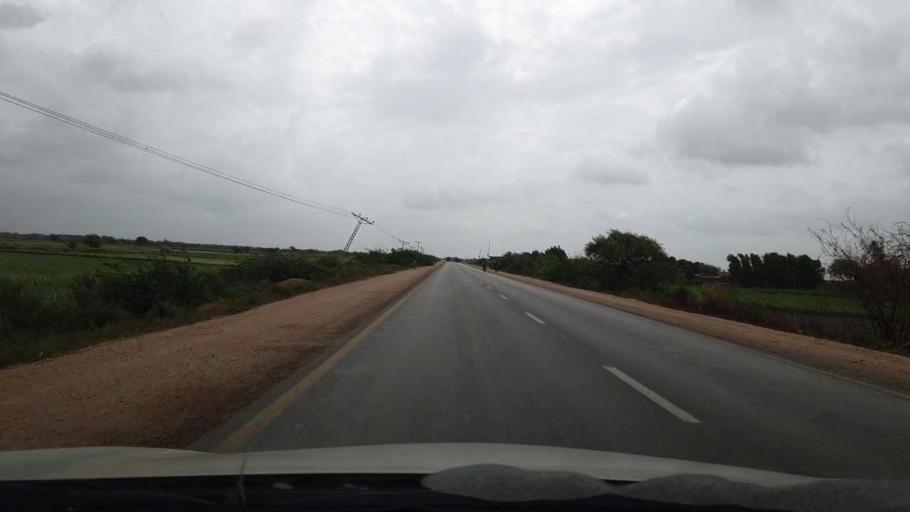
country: PK
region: Sindh
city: Mirpur Batoro
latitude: 24.6218
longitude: 68.3195
